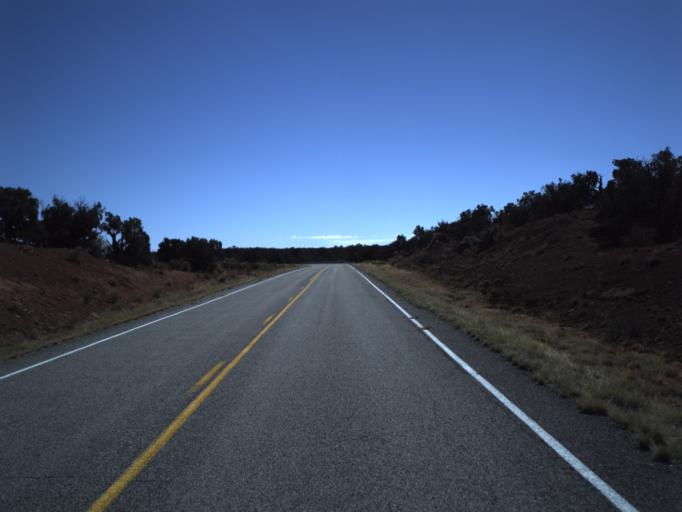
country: US
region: Utah
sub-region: San Juan County
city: Blanding
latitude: 37.5646
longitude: -110.0283
